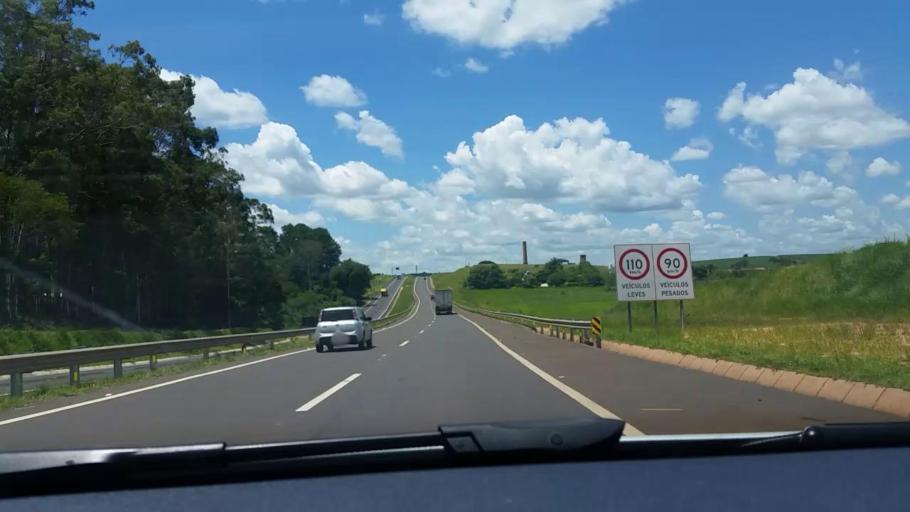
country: BR
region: Sao Paulo
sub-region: Bauru
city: Bauru
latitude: -22.4451
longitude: -49.1568
